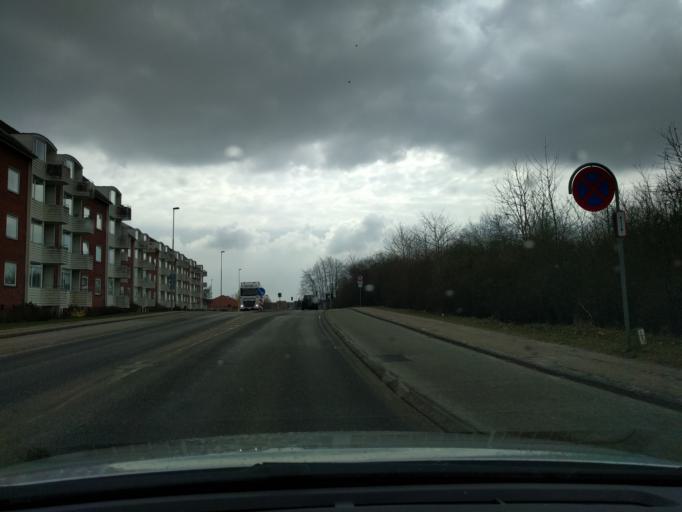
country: DK
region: South Denmark
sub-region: Odense Kommune
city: Odense
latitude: 55.4004
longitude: 10.3397
